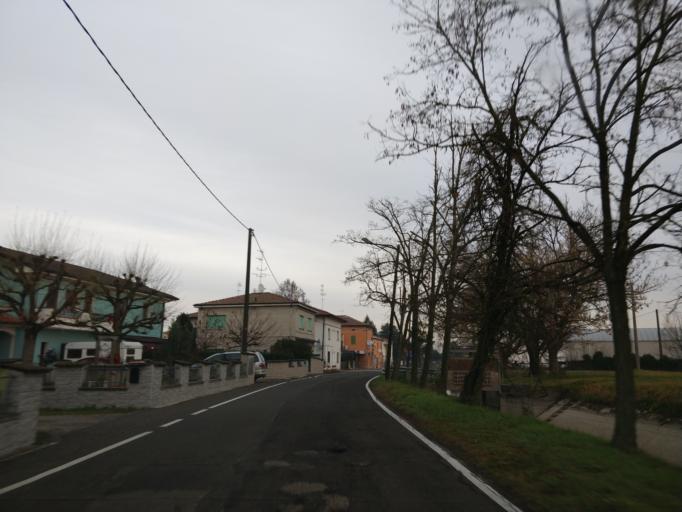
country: IT
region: Emilia-Romagna
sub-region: Provincia di Ferrara
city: Dosso
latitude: 44.7852
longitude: 11.3374
